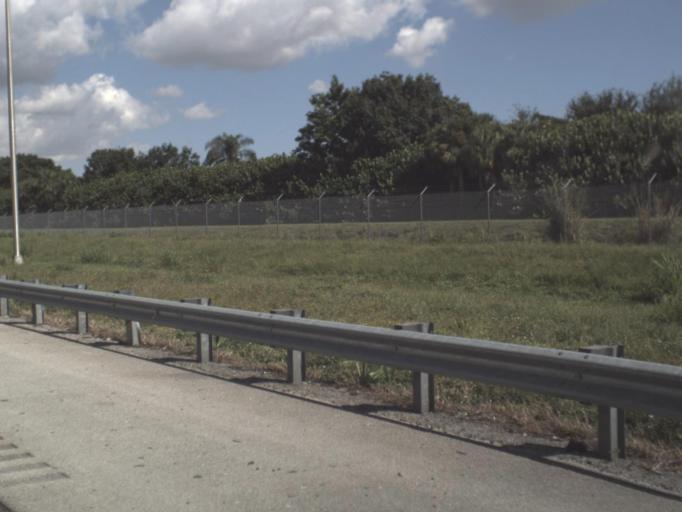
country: US
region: Florida
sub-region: Palm Beach County
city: Villages of Oriole
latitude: 26.5003
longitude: -80.1724
